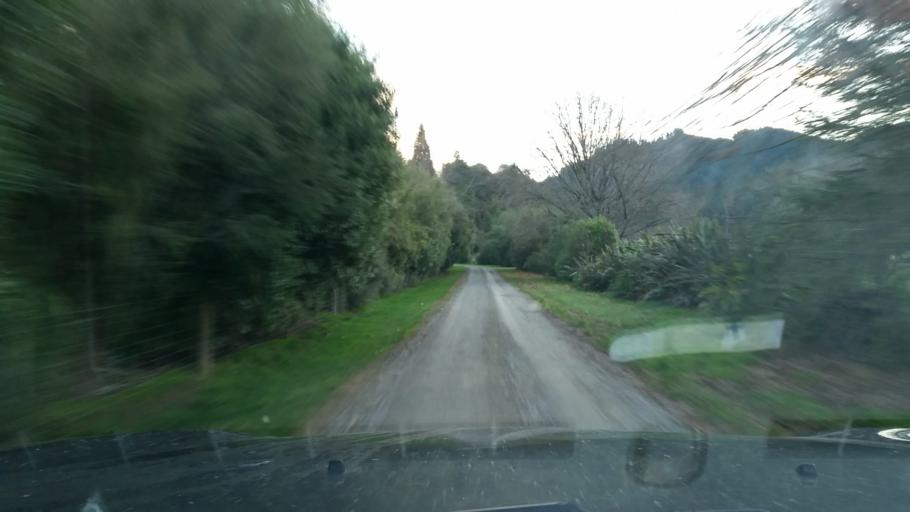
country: NZ
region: Marlborough
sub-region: Marlborough District
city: Blenheim
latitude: -41.4729
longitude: 173.7433
